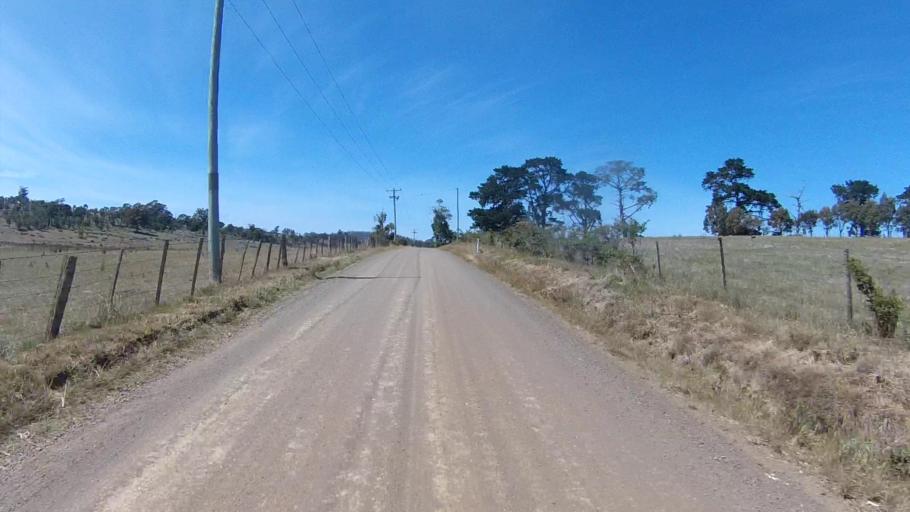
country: AU
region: Tasmania
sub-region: Sorell
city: Sorell
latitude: -42.7747
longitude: 147.6524
